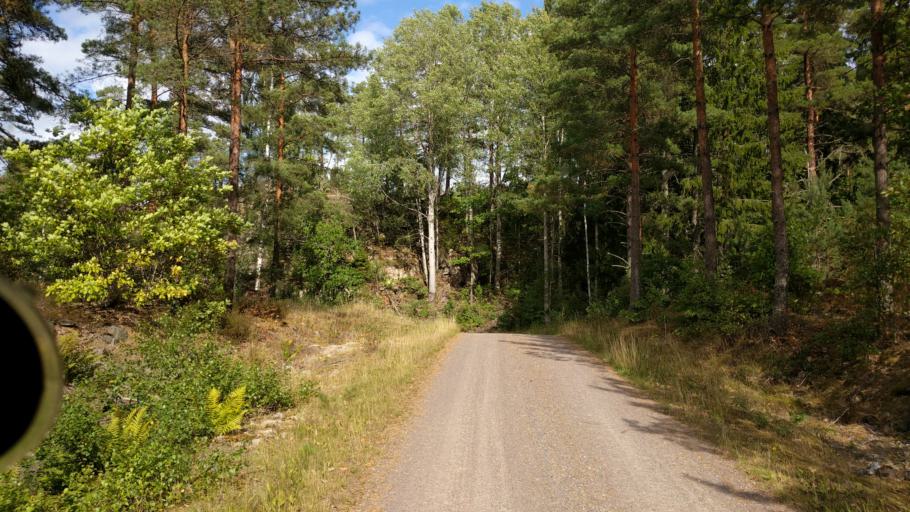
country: SE
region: Kalmar
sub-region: Vasterviks Kommun
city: Ankarsrum
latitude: 57.7183
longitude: 16.0911
